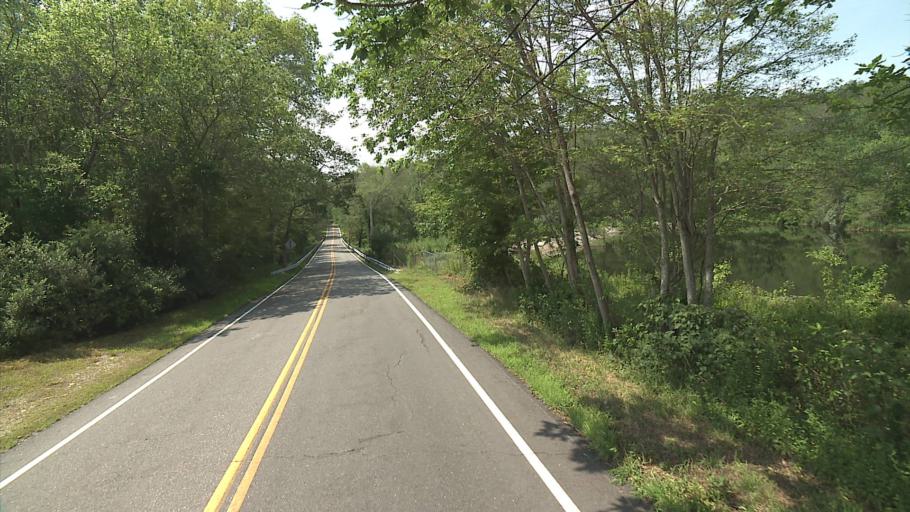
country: US
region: Connecticut
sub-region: Windham County
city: Danielson
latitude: 41.7601
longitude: -71.8496
